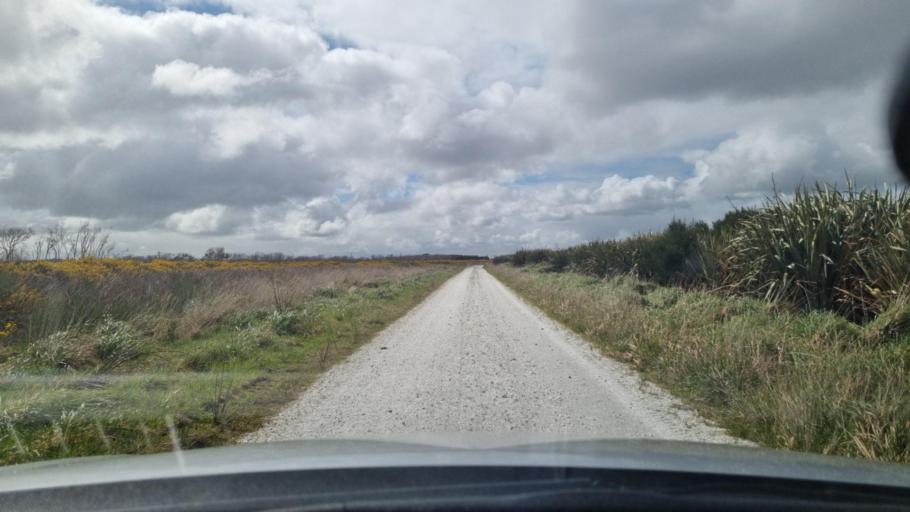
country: NZ
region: Southland
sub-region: Invercargill City
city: Bluff
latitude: -46.5317
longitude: 168.3052
